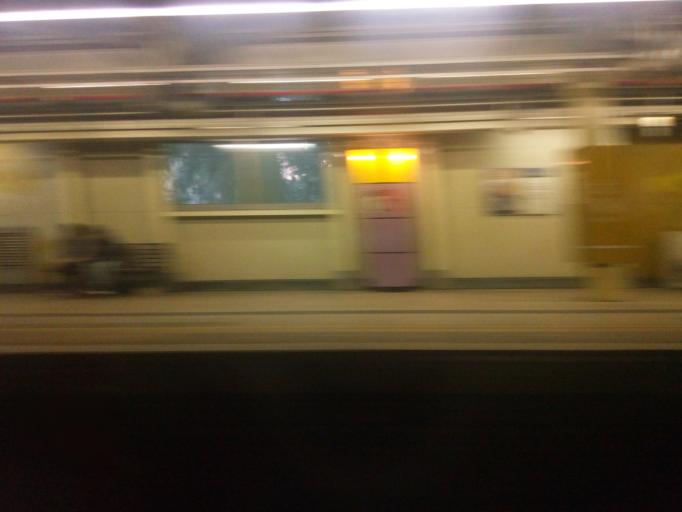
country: HK
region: Tai Po
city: Tai Po
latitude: 22.4503
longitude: 114.1614
